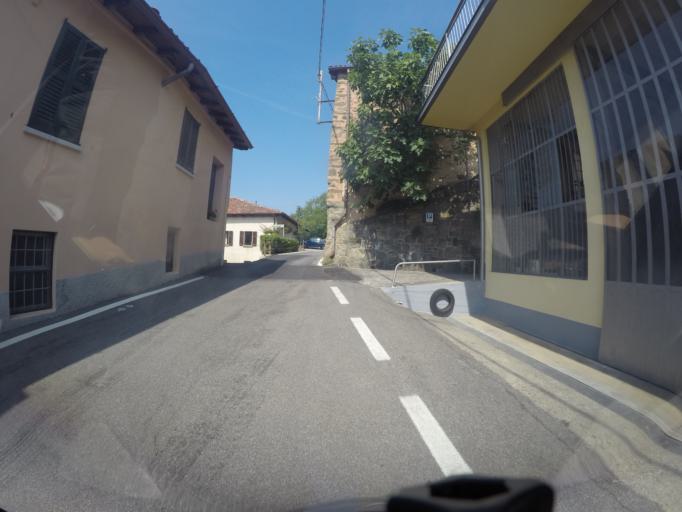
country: IT
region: Lombardy
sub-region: Provincia di Lecco
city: Santa Maria Hoe
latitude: 45.7515
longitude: 9.3876
